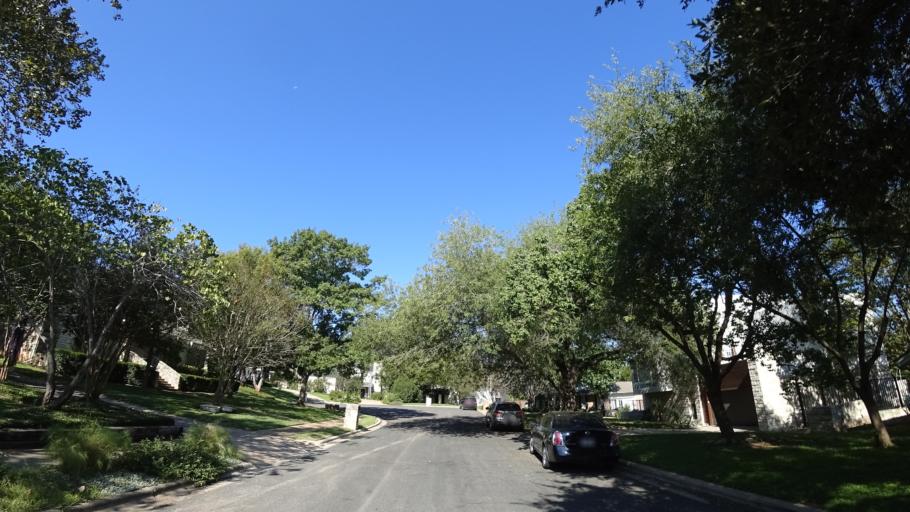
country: US
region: Texas
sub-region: Travis County
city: Rollingwood
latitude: 30.2674
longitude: -97.8071
